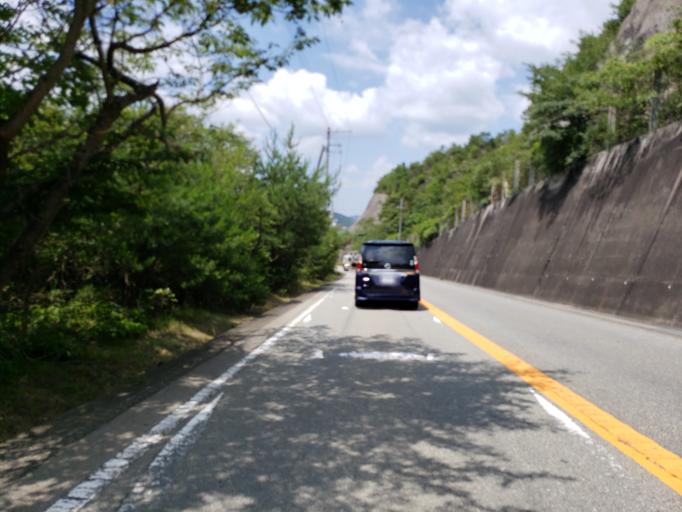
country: JP
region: Hyogo
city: Aioi
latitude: 34.7962
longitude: 134.4488
